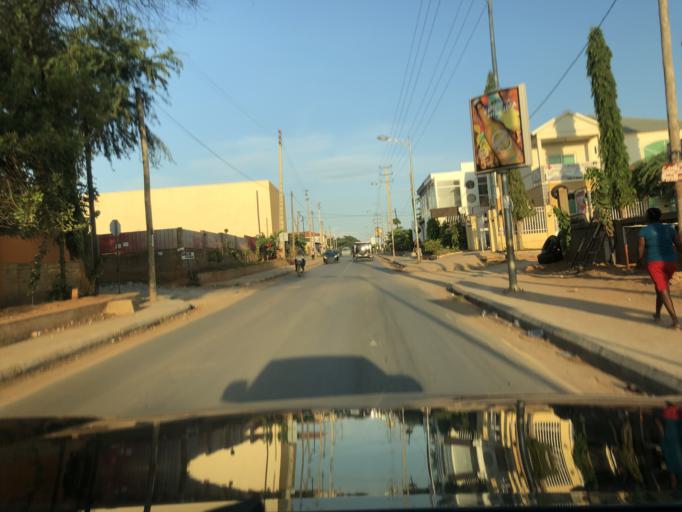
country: AO
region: Luanda
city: Luanda
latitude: -8.9512
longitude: 13.1737
